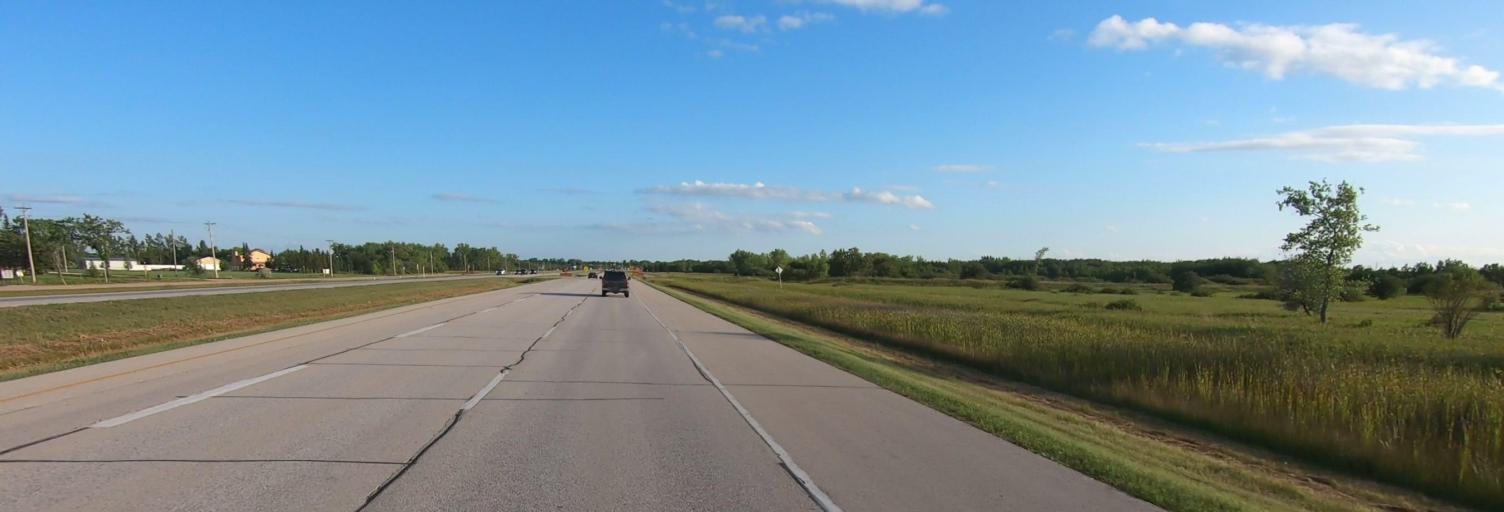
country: CA
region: Manitoba
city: Selkirk
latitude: 49.9840
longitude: -96.9756
